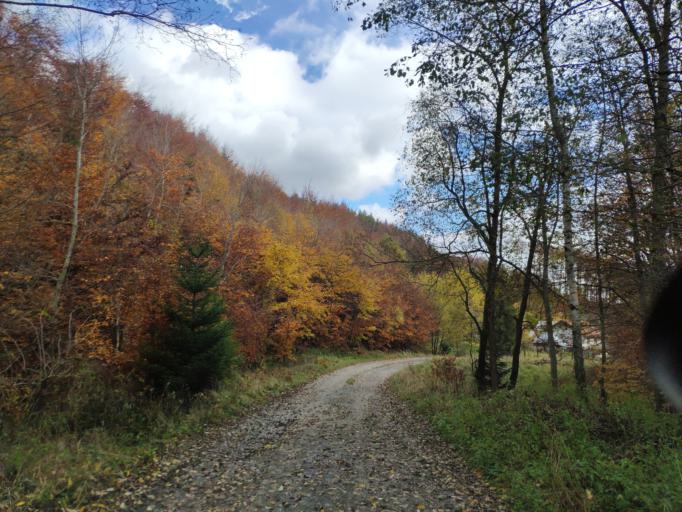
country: SK
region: Kosicky
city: Gelnica
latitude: 48.7593
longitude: 20.9861
